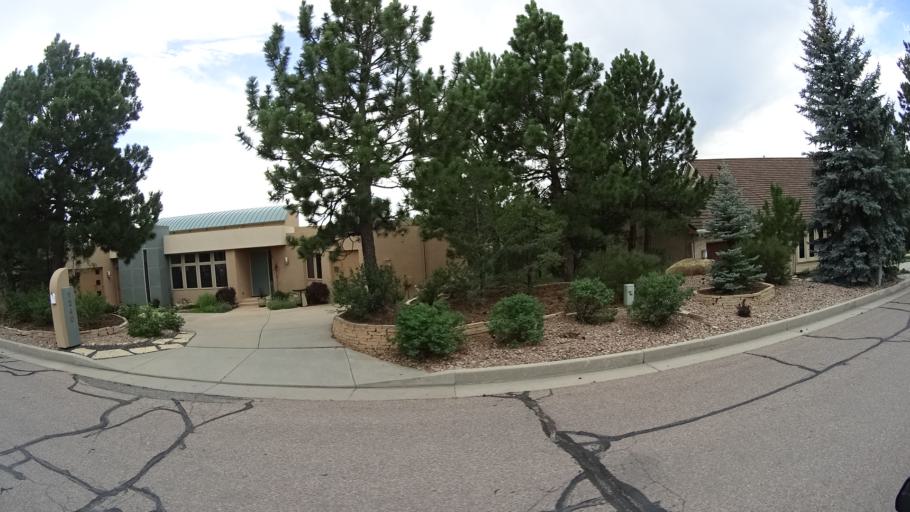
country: US
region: Colorado
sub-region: El Paso County
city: Colorado Springs
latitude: 38.9103
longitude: -104.8396
